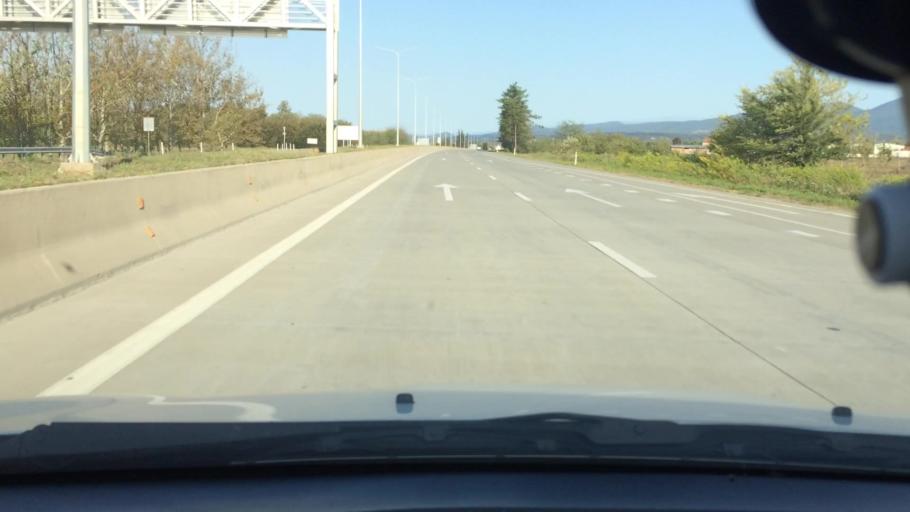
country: GE
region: Imereti
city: Zestap'oni
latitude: 42.1620
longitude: 42.9455
